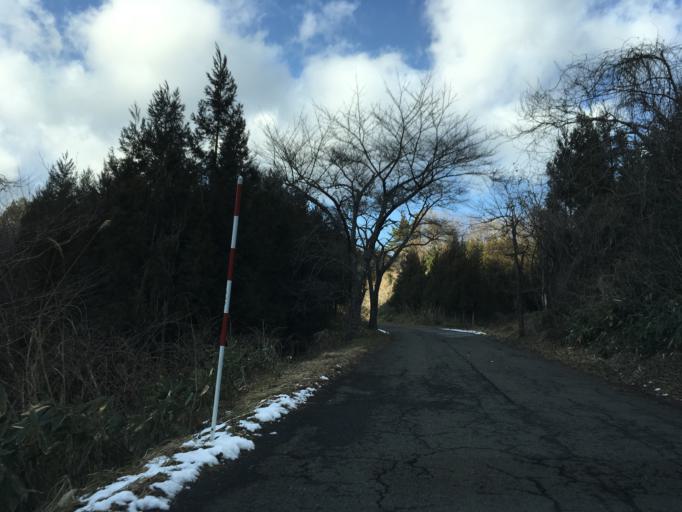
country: JP
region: Miyagi
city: Furukawa
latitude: 38.8170
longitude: 140.8329
